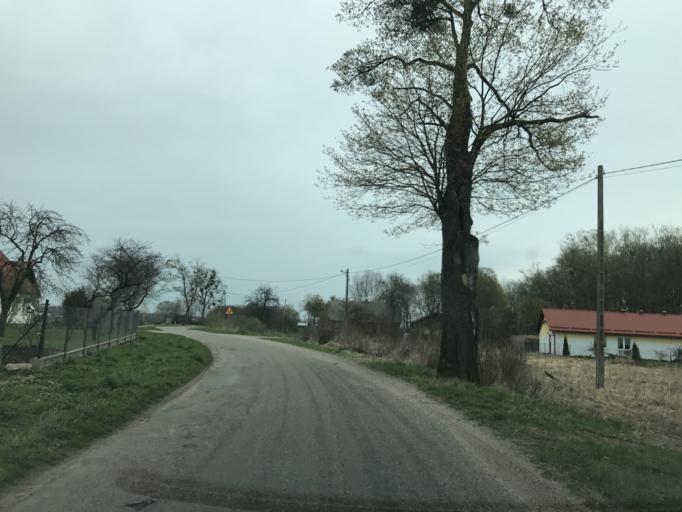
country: PL
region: Warmian-Masurian Voivodeship
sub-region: Powiat olsztynski
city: Olsztynek
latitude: 53.6286
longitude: 20.1724
